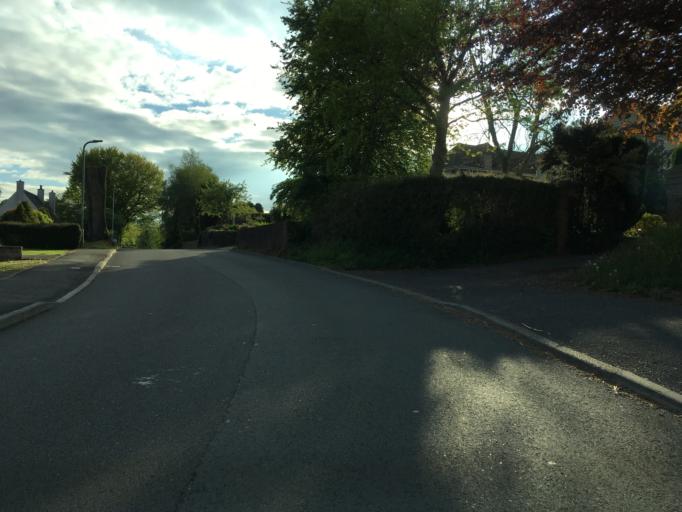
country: GB
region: Wales
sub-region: Monmouthshire
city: Chepstow
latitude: 51.6340
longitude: -2.6827
